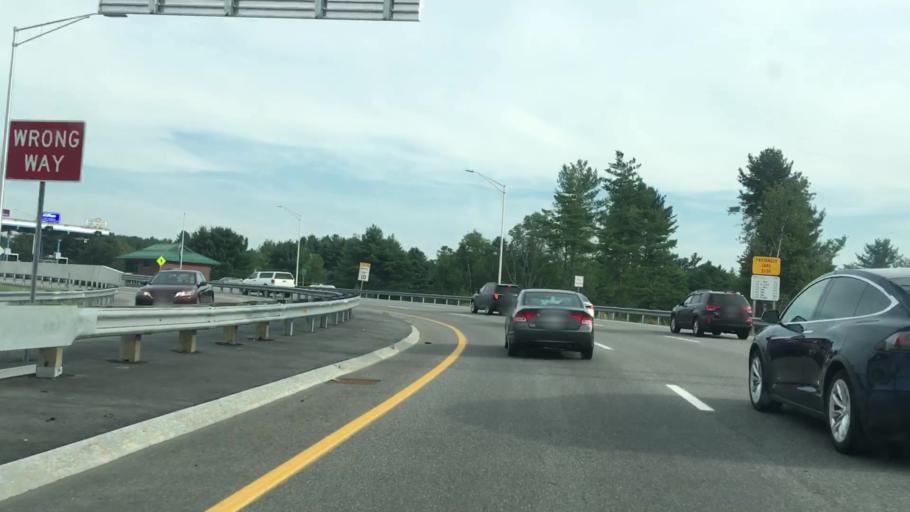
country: US
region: Maine
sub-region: Cumberland County
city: New Gloucester
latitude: 43.8822
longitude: -70.3386
